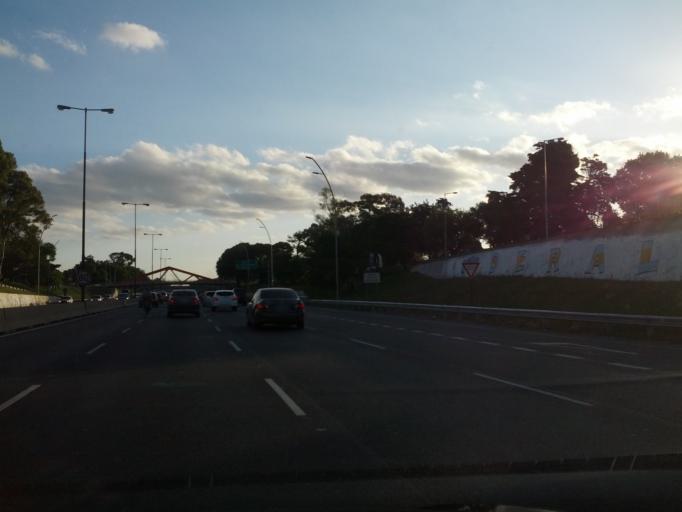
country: AR
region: Buenos Aires
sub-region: Partido de General San Martin
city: General San Martin
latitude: -34.5823
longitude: -58.5154
